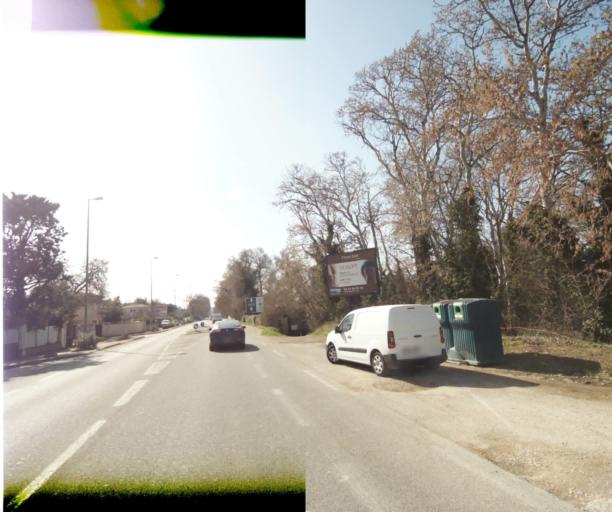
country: FR
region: Provence-Alpes-Cote d'Azur
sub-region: Departement des Bouches-du-Rhone
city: Bouc-Bel-Air
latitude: 43.4595
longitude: 5.4051
